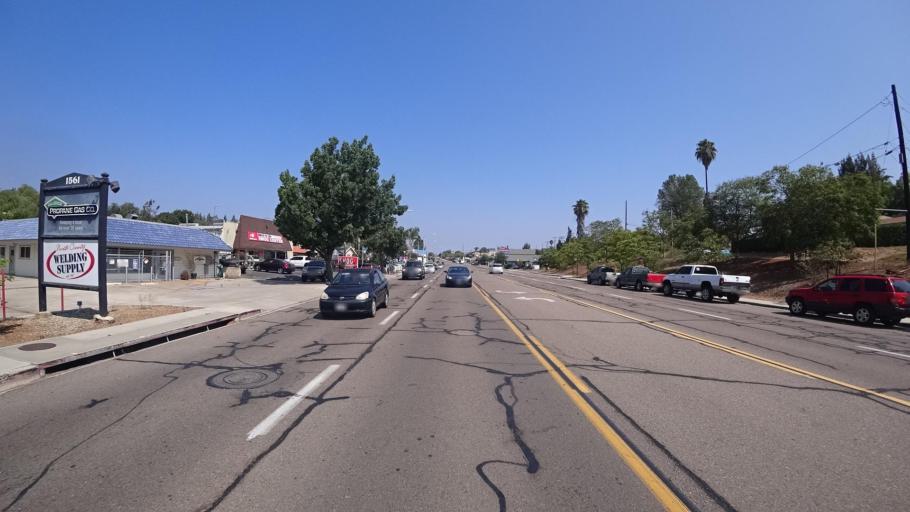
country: US
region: California
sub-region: San Diego County
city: Fallbrook
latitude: 33.3646
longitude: -117.2496
